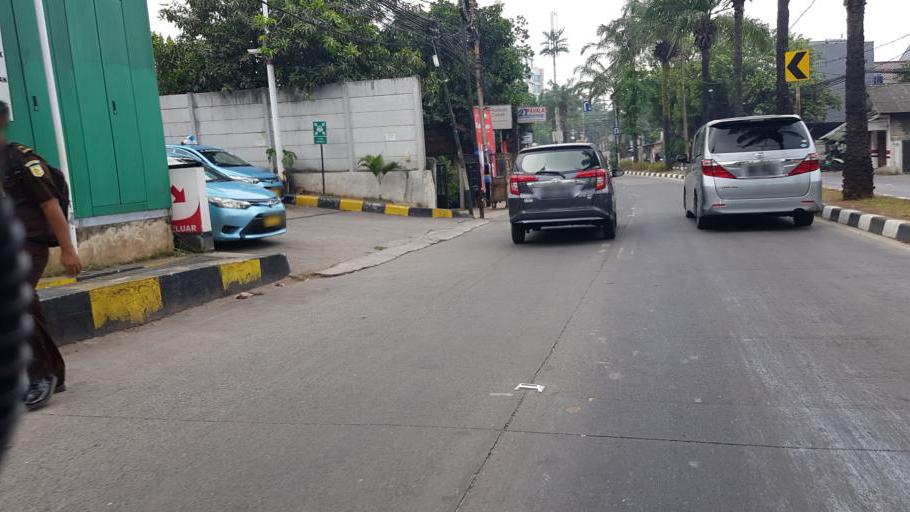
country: ID
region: Jakarta Raya
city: Jakarta
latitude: -6.3012
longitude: 106.8212
